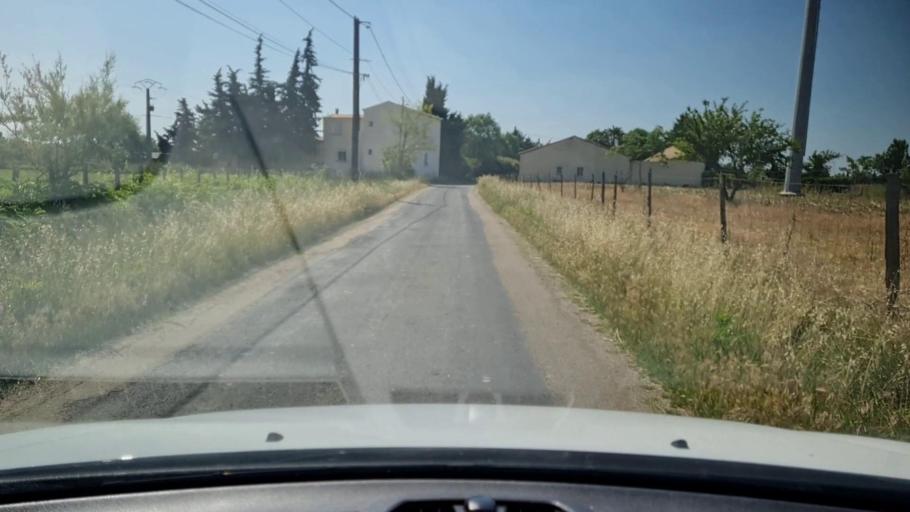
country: FR
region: Languedoc-Roussillon
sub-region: Departement du Gard
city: Le Cailar
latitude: 43.6617
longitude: 4.2331
